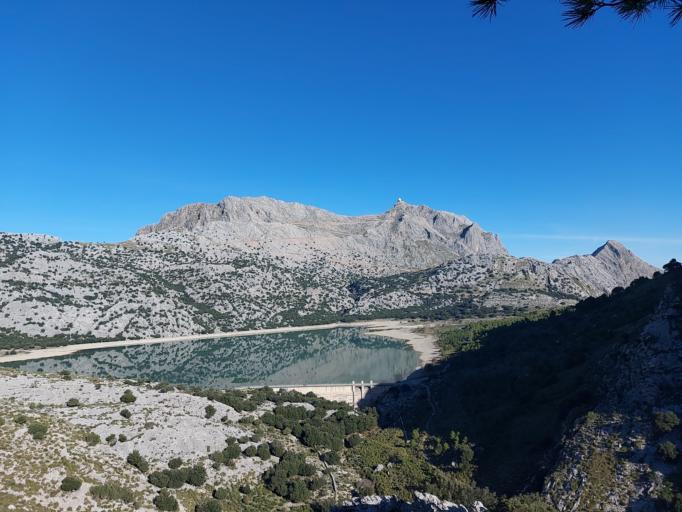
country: ES
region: Balearic Islands
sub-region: Illes Balears
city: Fornalutx
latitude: 39.7763
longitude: 2.7917
